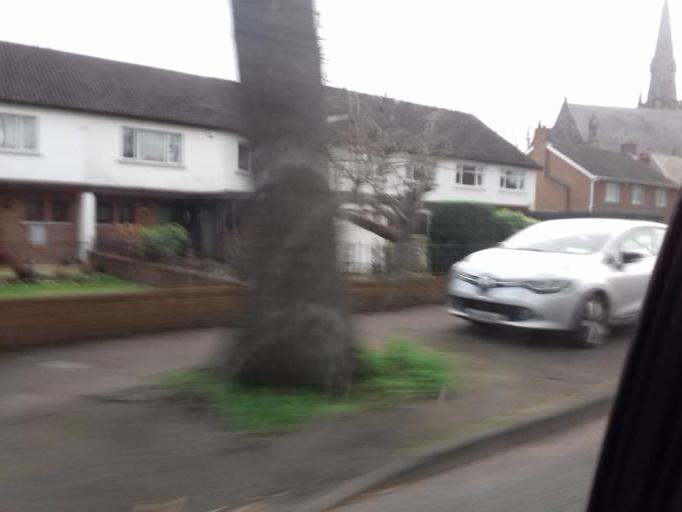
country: GB
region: Northern Ireland
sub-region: Newtownabbey District
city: Newtownabbey
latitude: 54.6277
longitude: -5.9366
